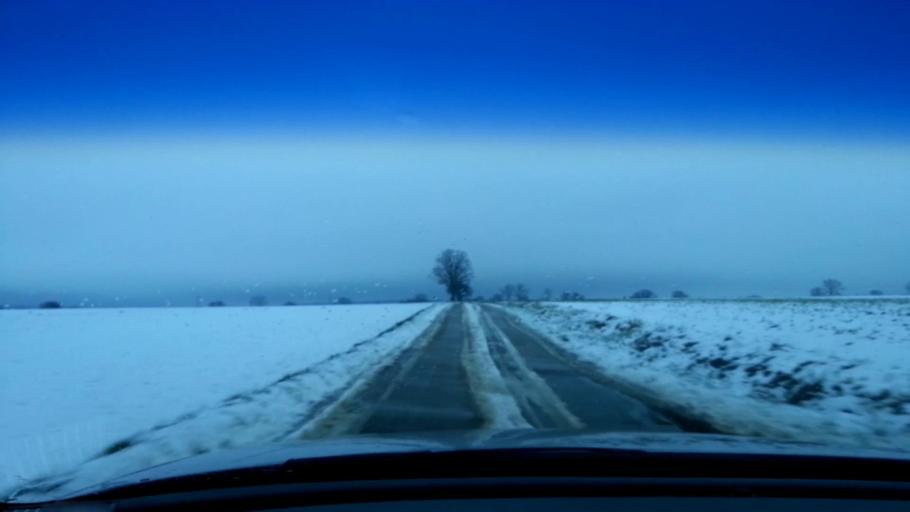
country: DE
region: Bavaria
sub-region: Upper Franconia
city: Litzendorf
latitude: 49.9498
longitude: 10.9961
